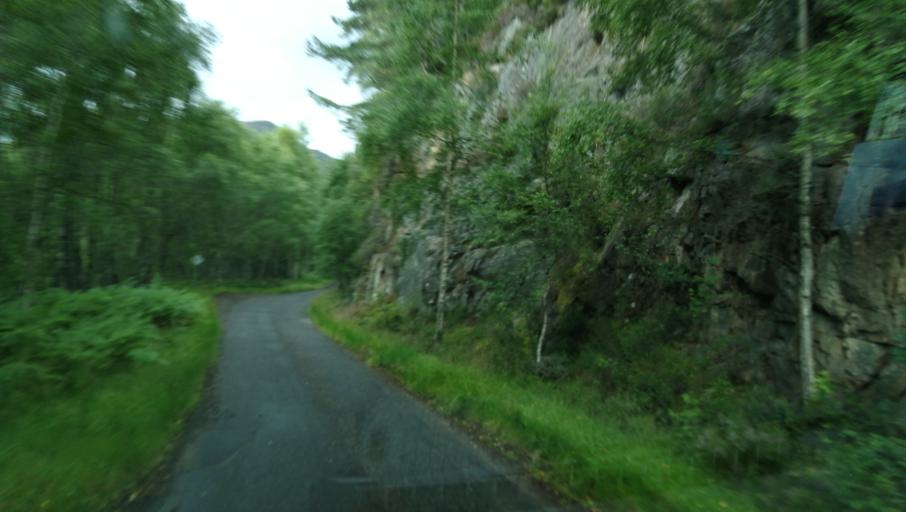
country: GB
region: Scotland
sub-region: Highland
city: Spean Bridge
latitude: 57.2959
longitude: -4.9090
